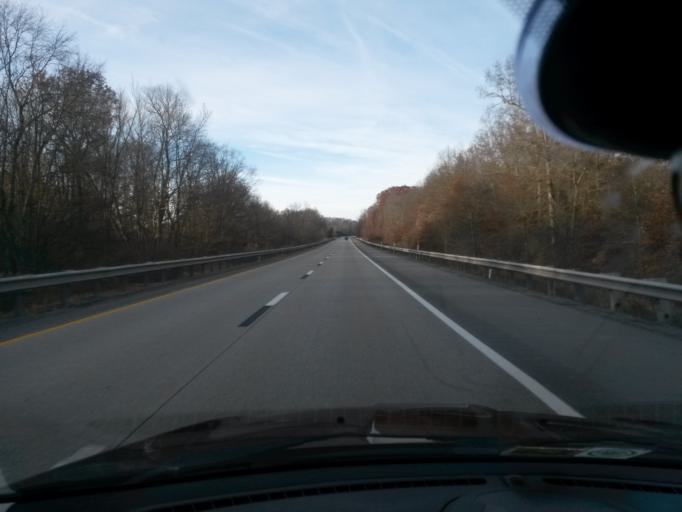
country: US
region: West Virginia
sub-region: Greenbrier County
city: Rainelle
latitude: 37.8942
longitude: -80.6573
